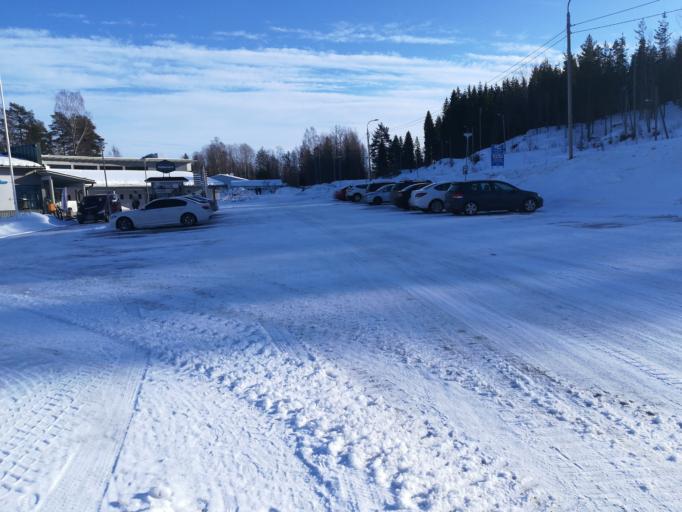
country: FI
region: Southern Savonia
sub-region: Savonlinna
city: Savonlinna
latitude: 61.8081
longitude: 29.0734
